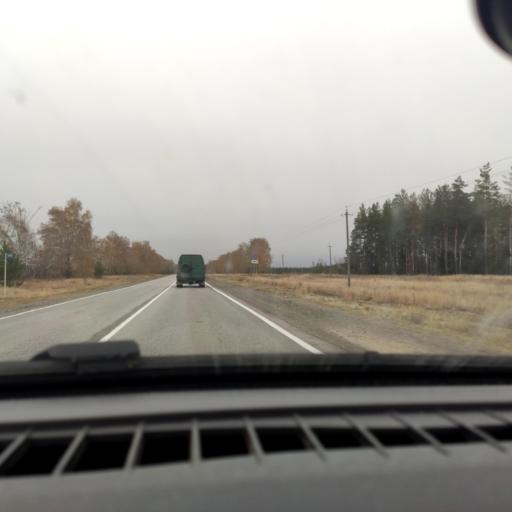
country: RU
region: Voronezj
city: Uryv-Pokrovka
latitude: 51.0591
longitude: 38.9909
